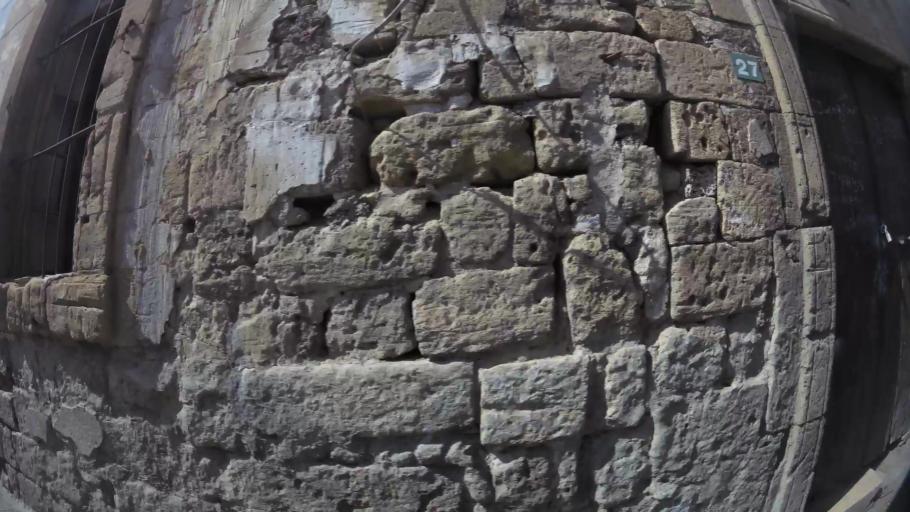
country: CY
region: Lefkosia
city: Nicosia
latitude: 35.1780
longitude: 33.3661
